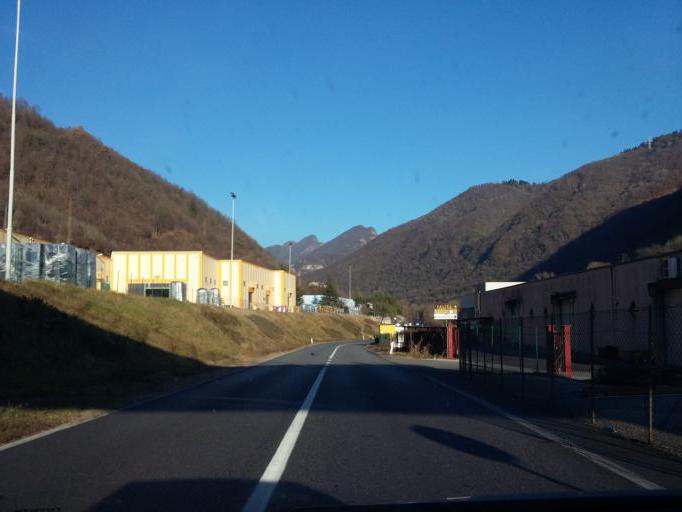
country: IT
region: Lombardy
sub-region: Provincia di Brescia
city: Lavenone
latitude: 45.7203
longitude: 10.4212
